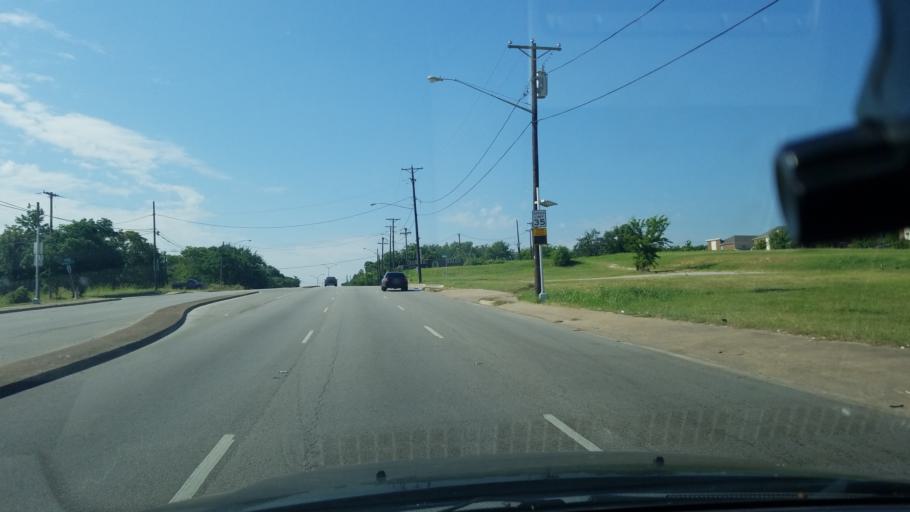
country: US
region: Texas
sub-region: Dallas County
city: Dallas
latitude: 32.7465
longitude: -96.7996
